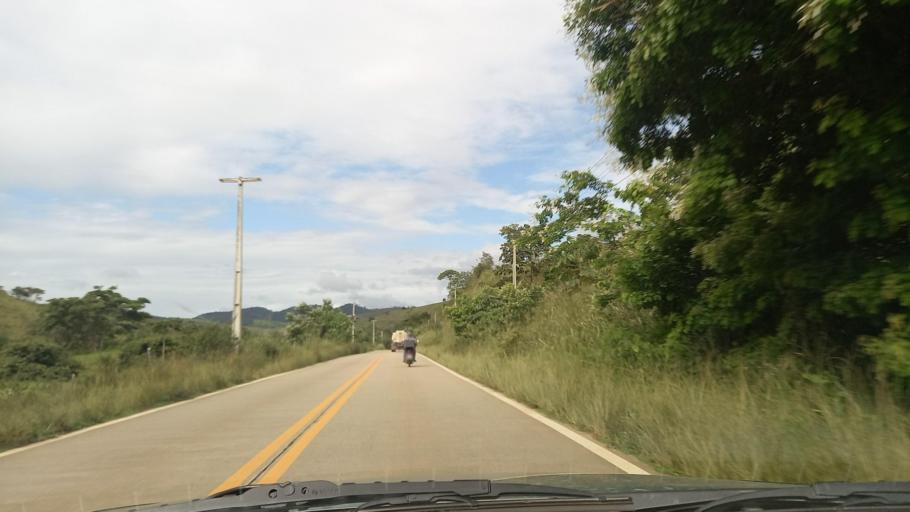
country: BR
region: Pernambuco
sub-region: Maraial
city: Maraial
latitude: -8.7502
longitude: -35.8294
